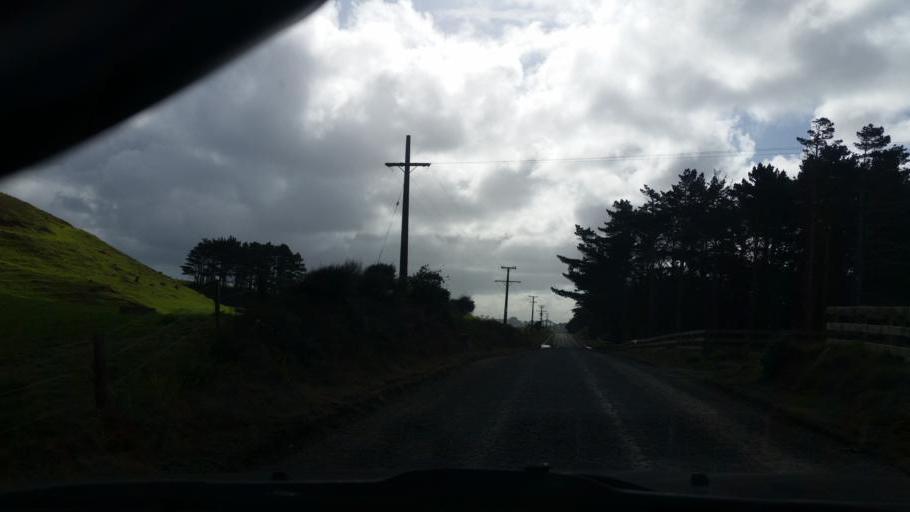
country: NZ
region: Northland
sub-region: Kaipara District
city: Dargaville
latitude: -36.0615
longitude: 173.8765
